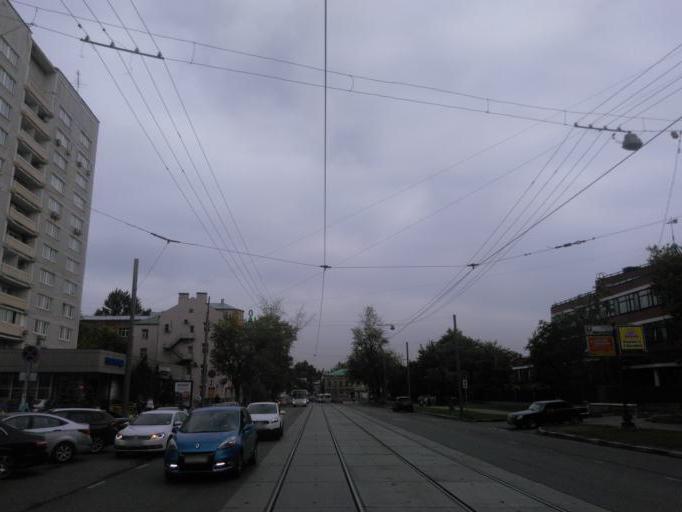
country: RU
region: Moscow
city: Zamoskvorech'ye
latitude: 55.7252
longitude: 37.6370
